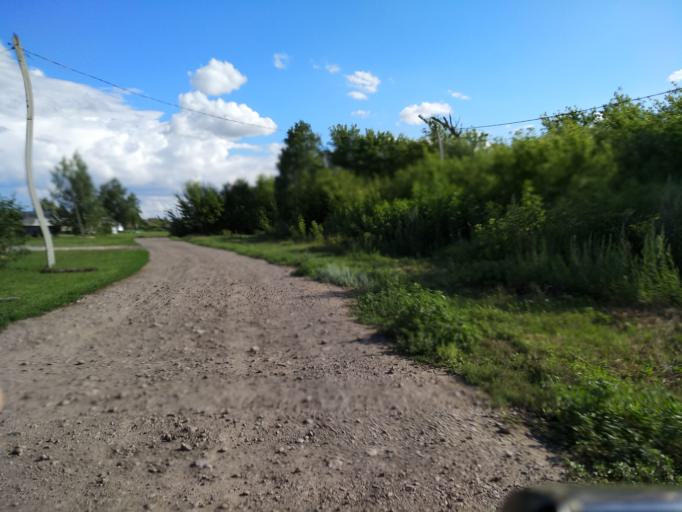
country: RU
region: Lipetsk
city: Dobrinka
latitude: 52.0311
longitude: 40.5626
